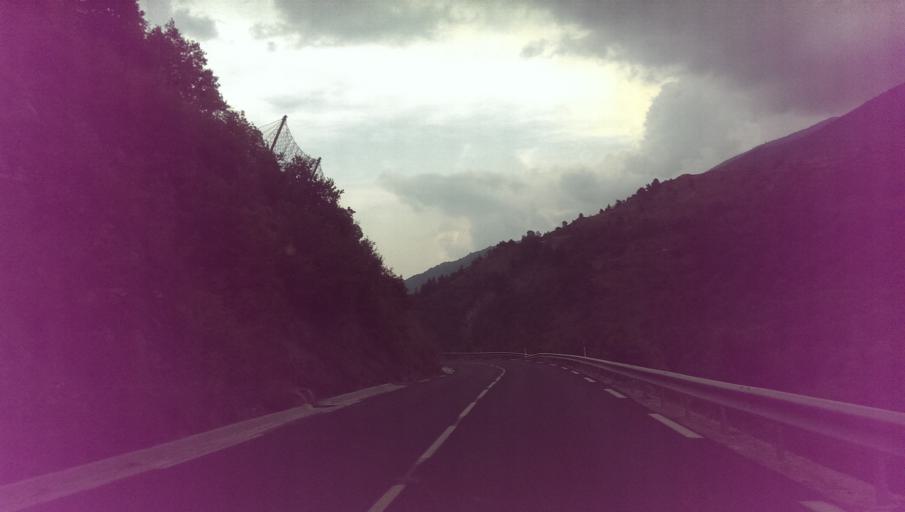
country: ES
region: Catalonia
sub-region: Provincia de Girona
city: Llivia
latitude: 42.5062
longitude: 2.1721
